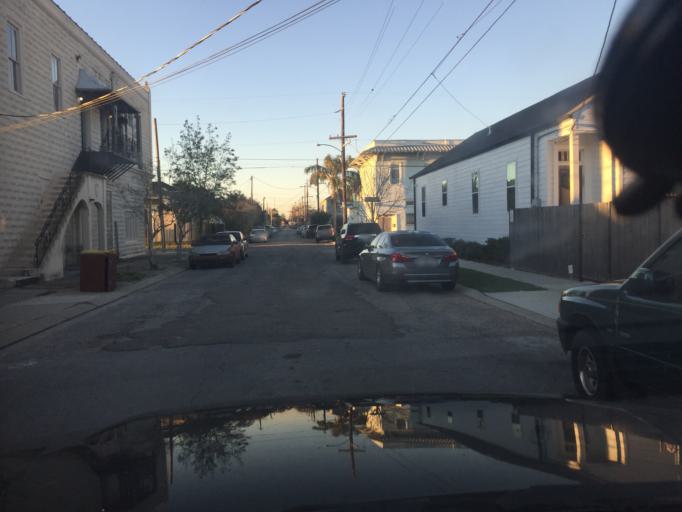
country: US
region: Louisiana
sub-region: Orleans Parish
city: New Orleans
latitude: 29.9756
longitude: -90.0859
